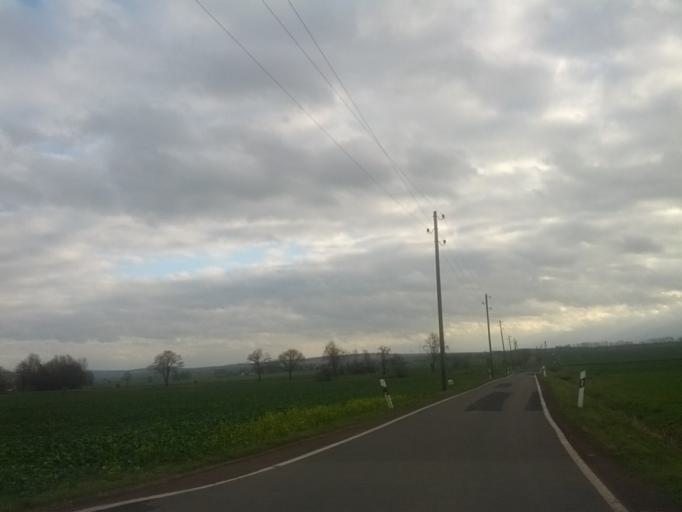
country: DE
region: Thuringia
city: Haina
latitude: 51.0198
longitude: 10.4770
